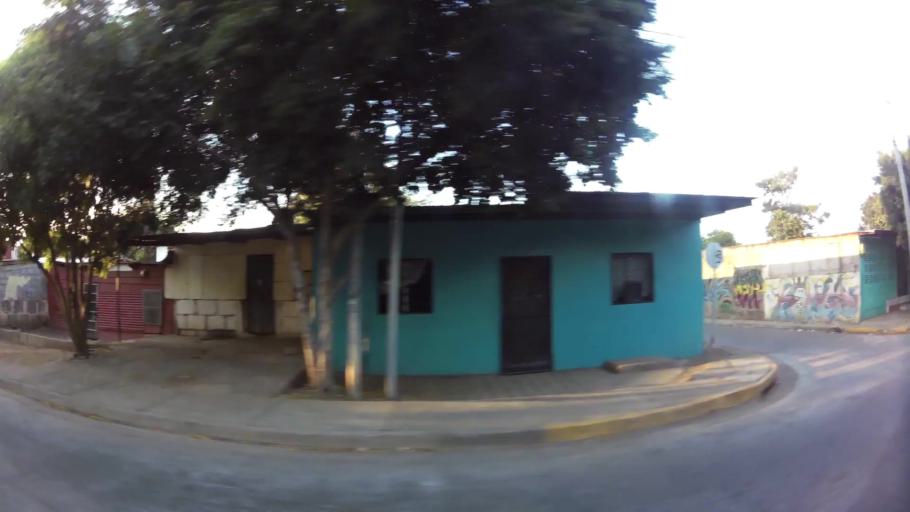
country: NI
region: Managua
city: Managua
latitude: 12.1374
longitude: -86.2372
